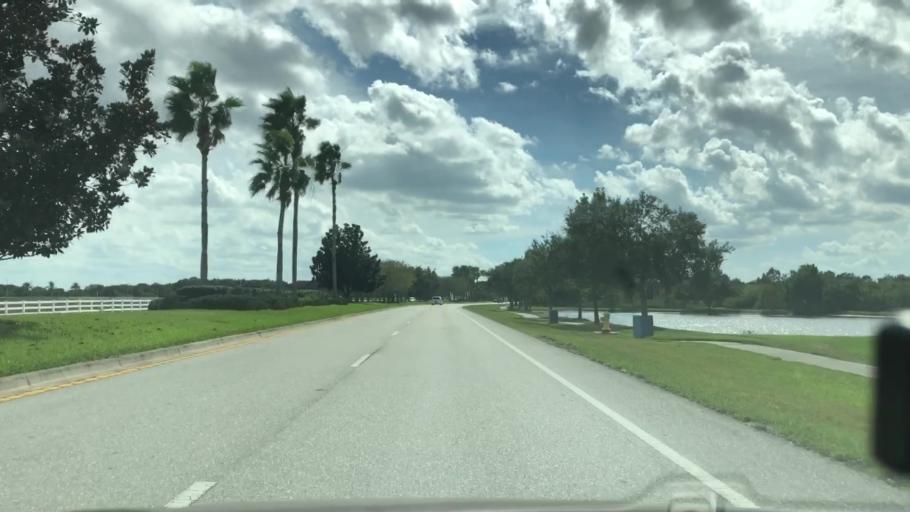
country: US
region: Florida
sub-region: Sarasota County
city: The Meadows
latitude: 27.3996
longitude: -82.3990
